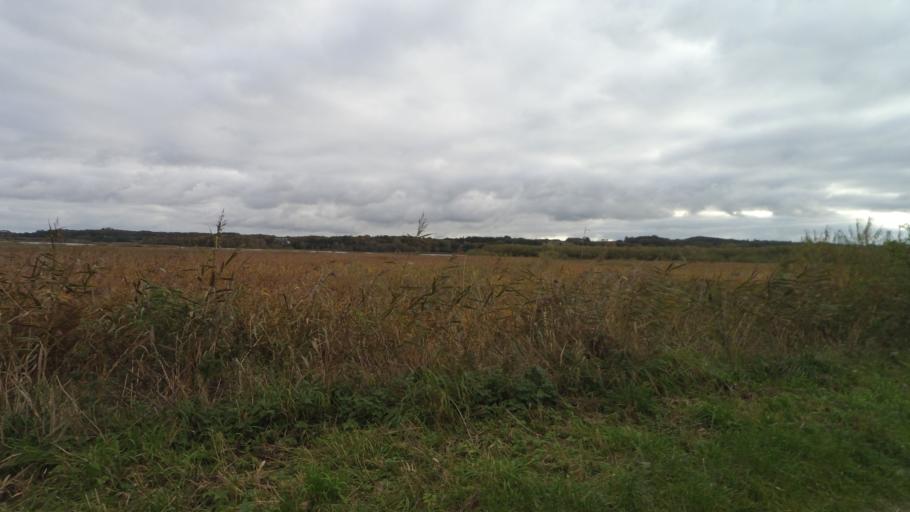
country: DK
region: Central Jutland
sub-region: Arhus Kommune
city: Kolt
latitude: 56.1441
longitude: 10.0624
